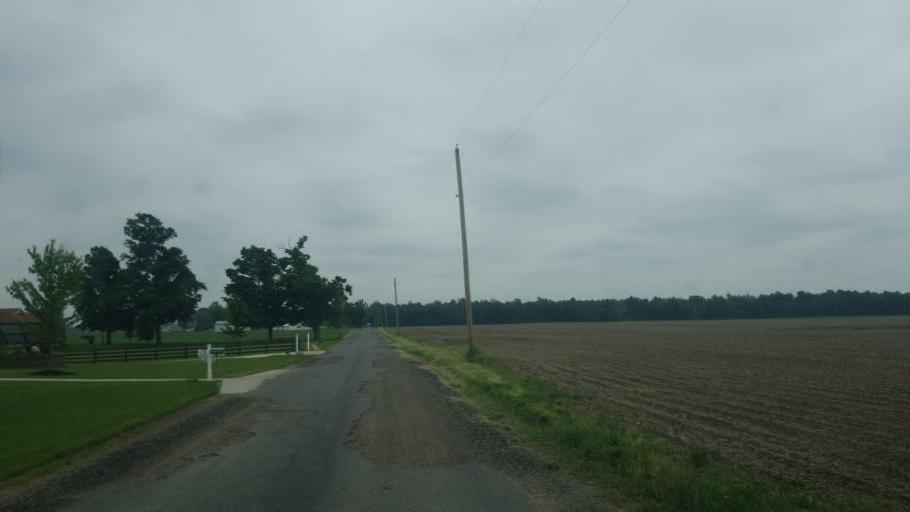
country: US
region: Indiana
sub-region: Elkhart County
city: Wakarusa
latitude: 41.4892
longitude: -86.0595
